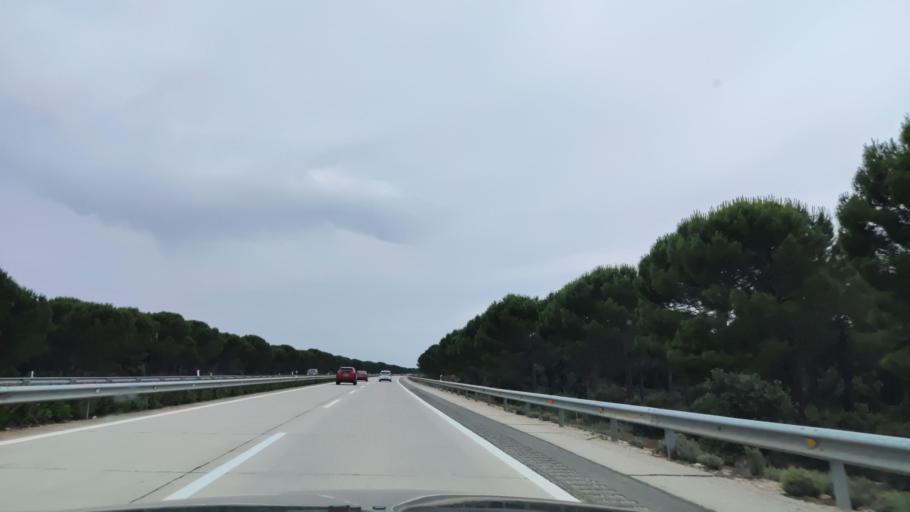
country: ES
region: Castille-La Mancha
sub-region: Provincia de Cuenca
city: Pozoamargo
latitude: 39.3422
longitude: -2.1996
